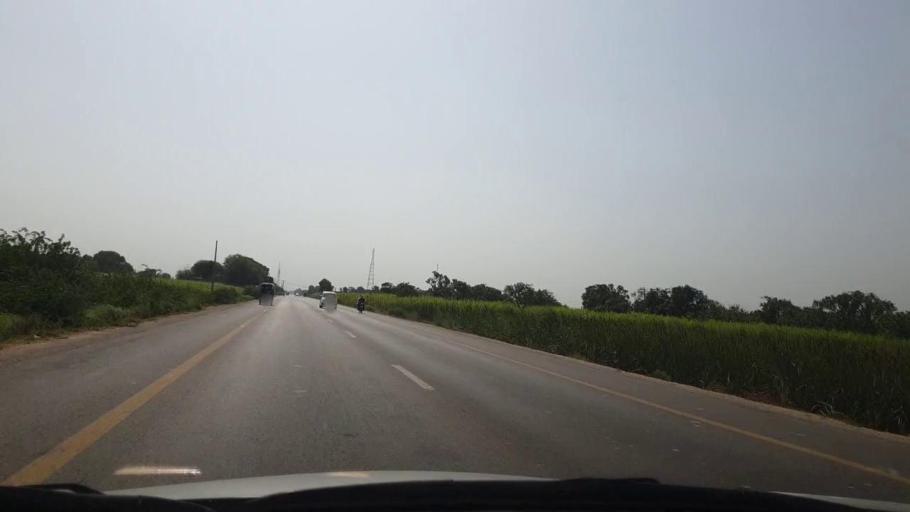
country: PK
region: Sindh
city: Tando Muhammad Khan
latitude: 25.0992
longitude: 68.5916
